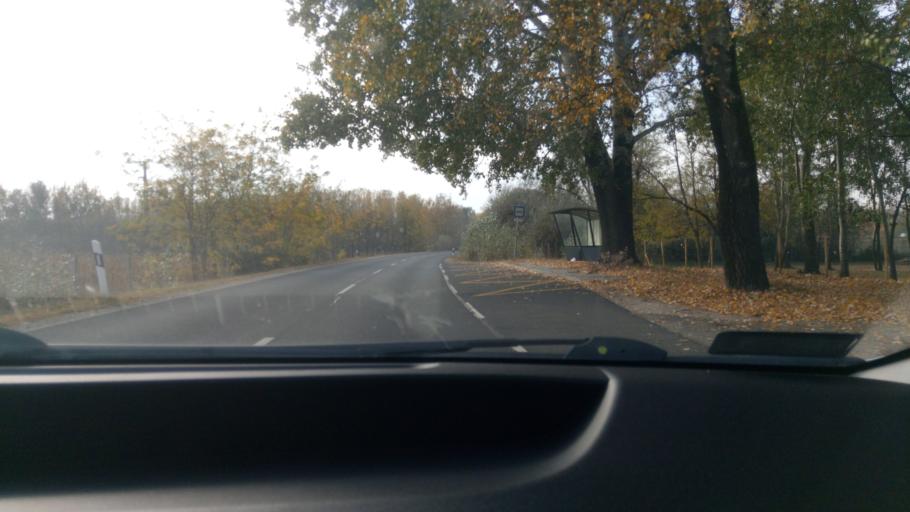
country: HU
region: Bacs-Kiskun
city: Jaszszentlaszlo
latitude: 46.5442
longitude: 19.7419
